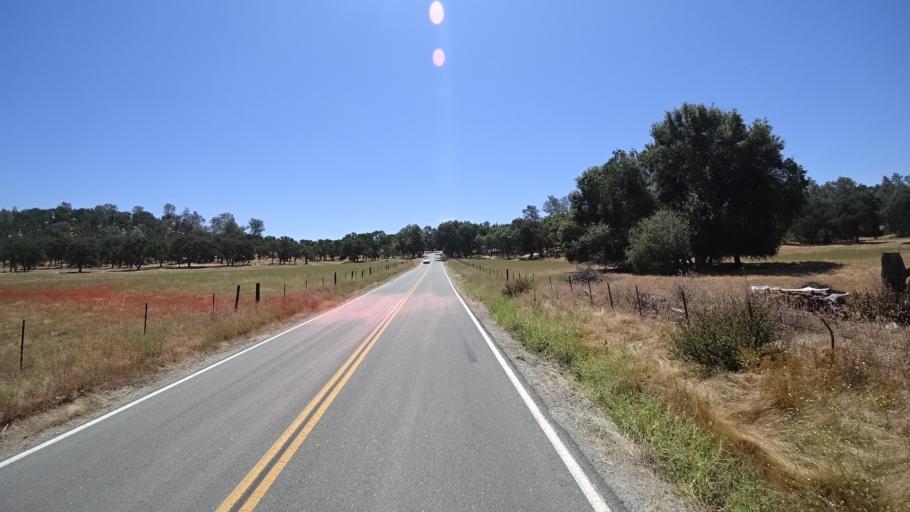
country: US
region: California
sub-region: Calaveras County
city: Rancho Calaveras
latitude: 38.1347
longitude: -120.8793
